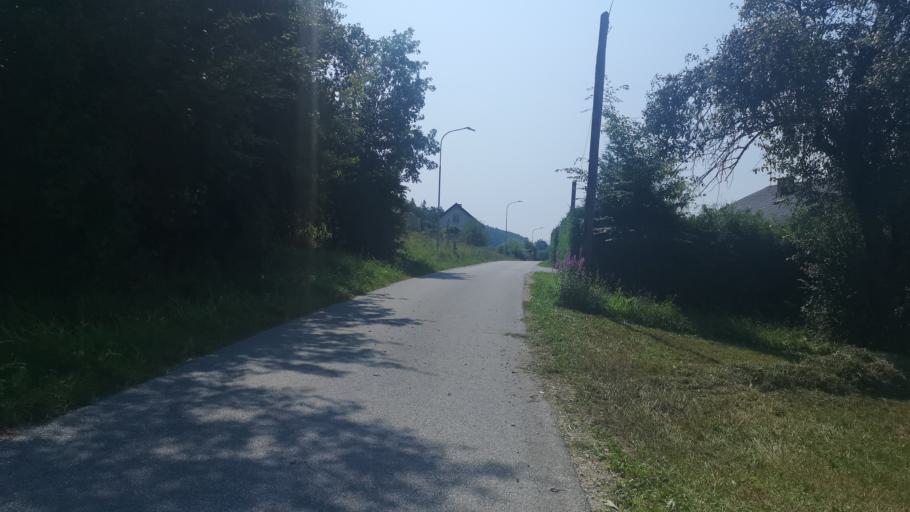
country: AT
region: Styria
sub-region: Politischer Bezirk Deutschlandsberg
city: Lannach
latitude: 46.9339
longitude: 15.3431
